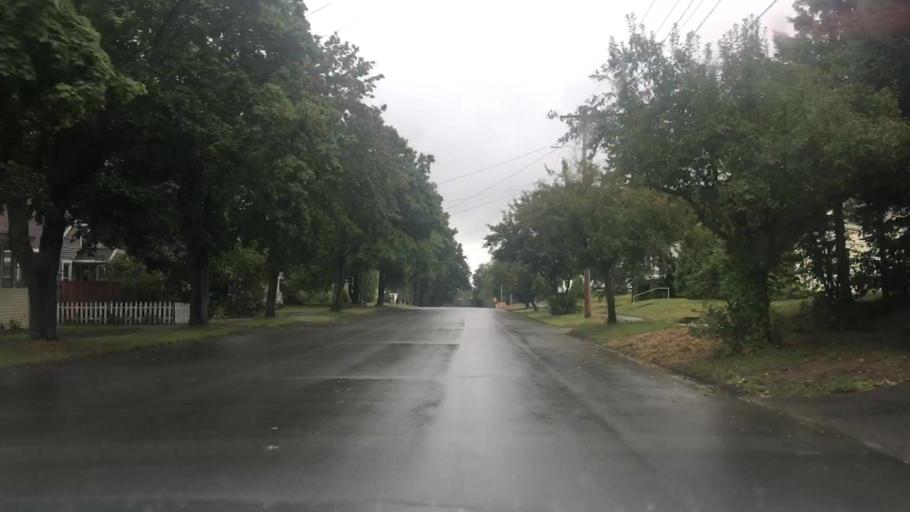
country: US
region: Maine
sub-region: Penobscot County
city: Brewer
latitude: 44.8164
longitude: -68.7602
